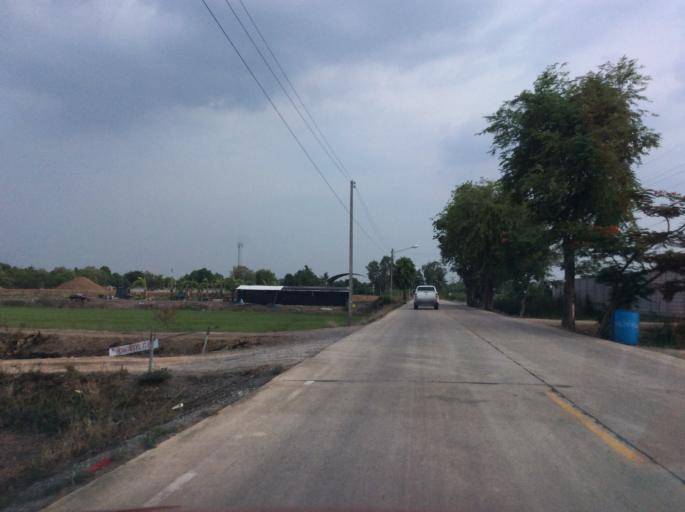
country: TH
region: Pathum Thani
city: Thanyaburi
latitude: 13.9770
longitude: 100.7266
